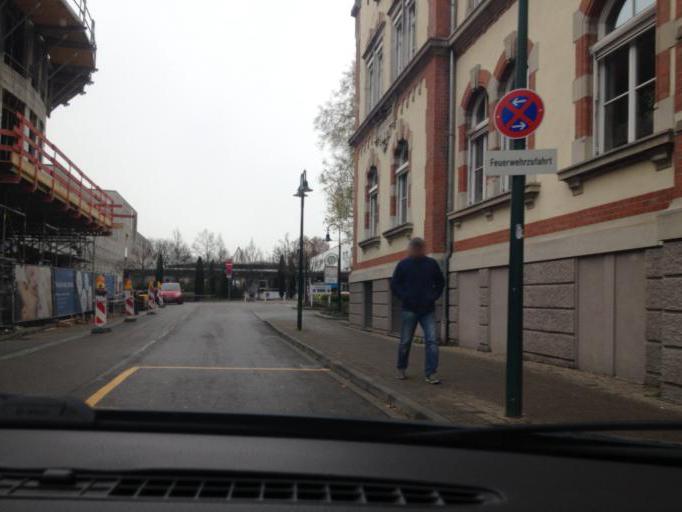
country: DE
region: Baden-Wuerttemberg
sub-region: Regierungsbezirk Stuttgart
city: Ludwigsburg
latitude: 48.8979
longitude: 9.2041
